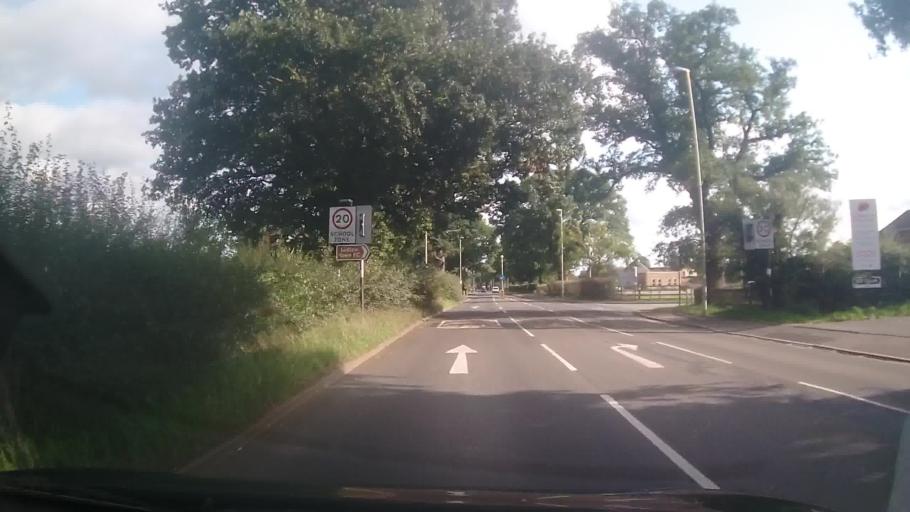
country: GB
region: England
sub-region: Shropshire
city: Ludlow
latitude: 52.3799
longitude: -2.7282
